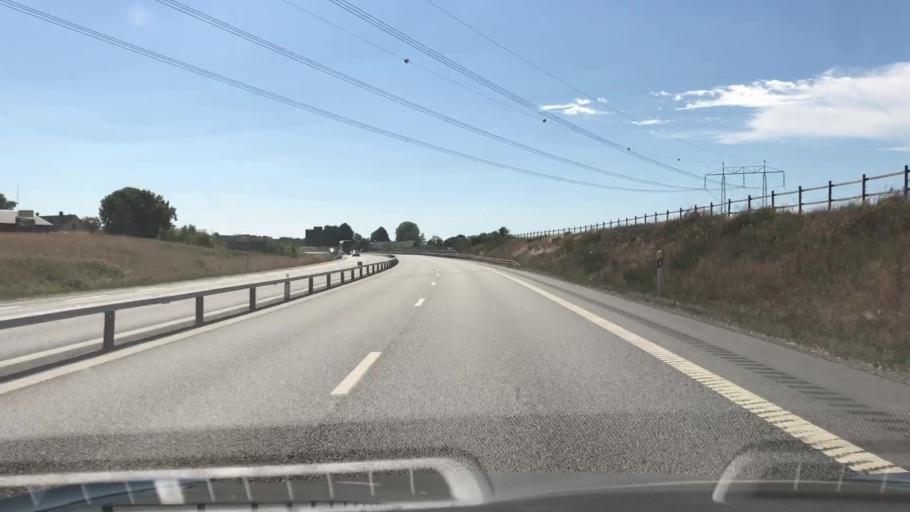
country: SE
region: Skane
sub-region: Hoors Kommun
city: Loberod
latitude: 55.8036
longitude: 13.4572
